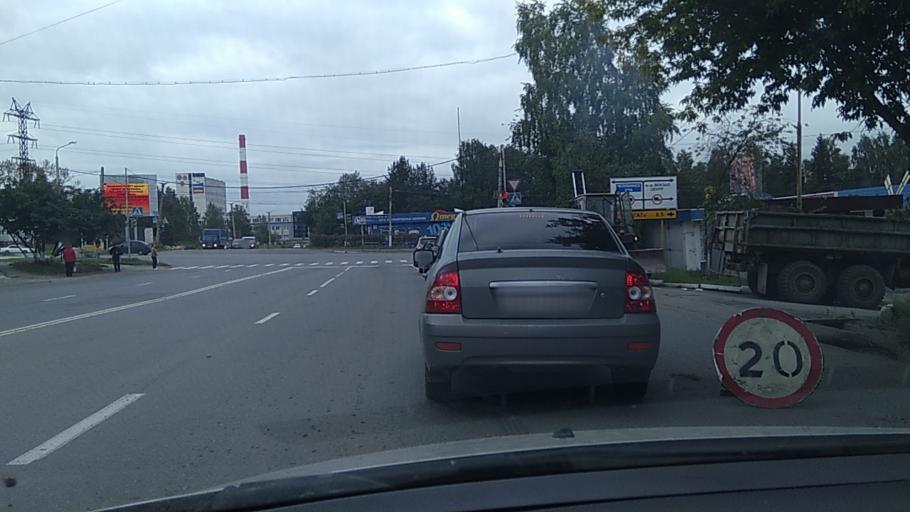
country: RU
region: Chelyabinsk
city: Zlatoust
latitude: 55.1140
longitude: 59.7077
